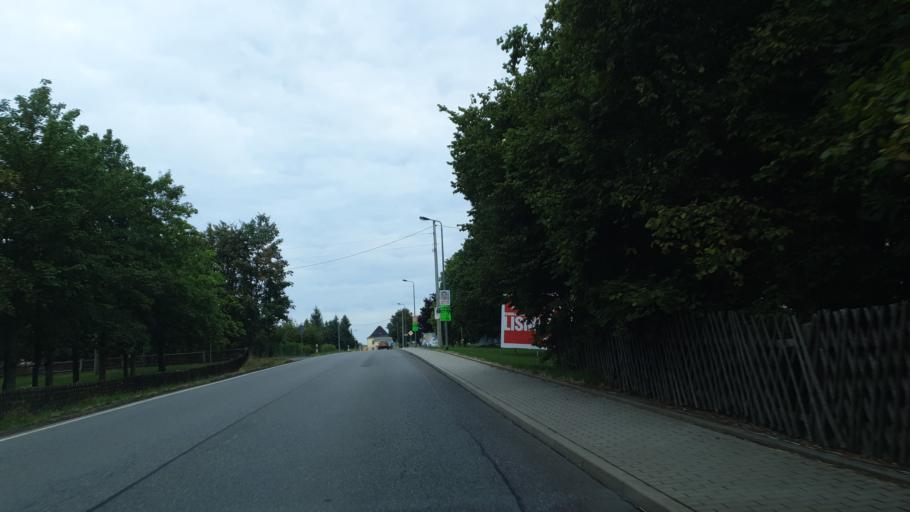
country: DE
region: Saxony
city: Callenberg
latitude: 50.8479
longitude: 12.6364
